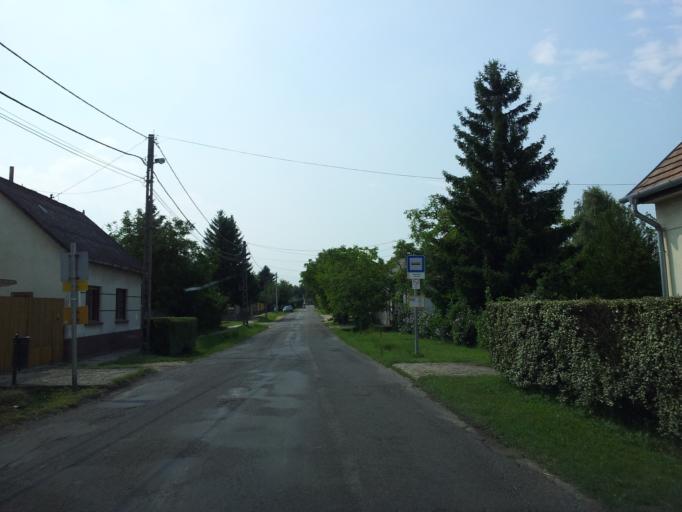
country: HU
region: Pest
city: Szigetujfalu
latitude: 47.2323
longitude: 18.9326
